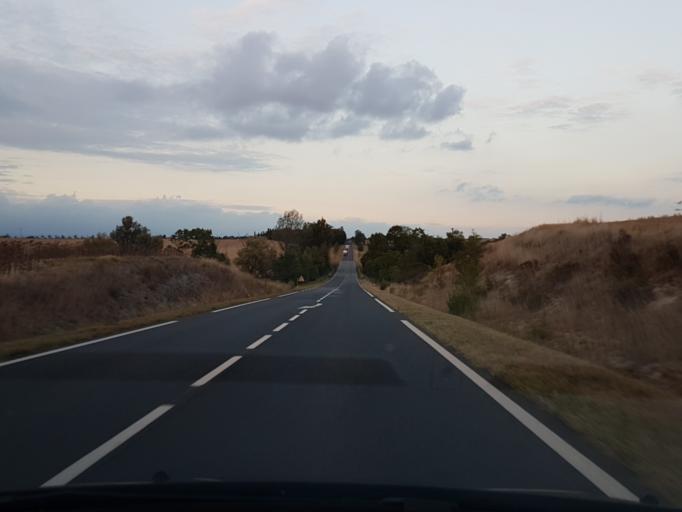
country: FR
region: Languedoc-Roussillon
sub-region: Departement de l'Aude
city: Bram
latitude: 43.1736
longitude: 2.0086
